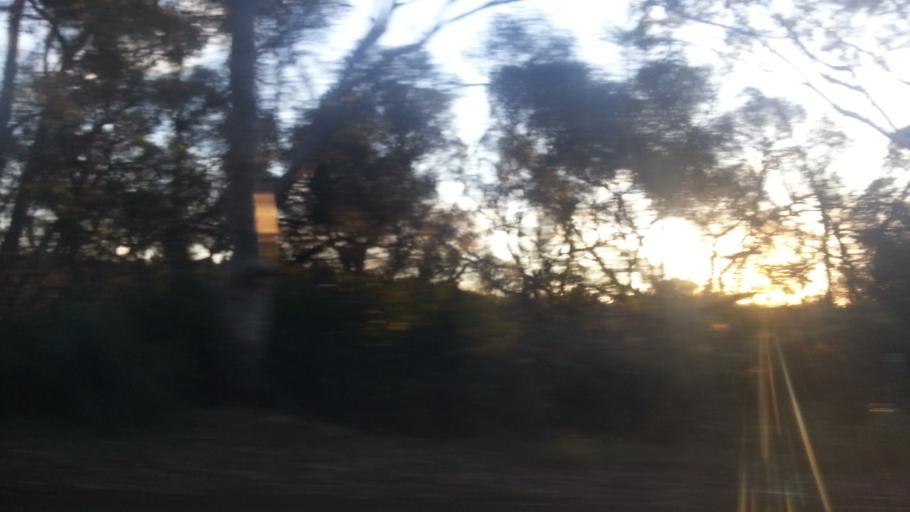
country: AU
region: New South Wales
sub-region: Wollongong
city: Mount Keira
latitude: -34.3809
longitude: 150.8337
